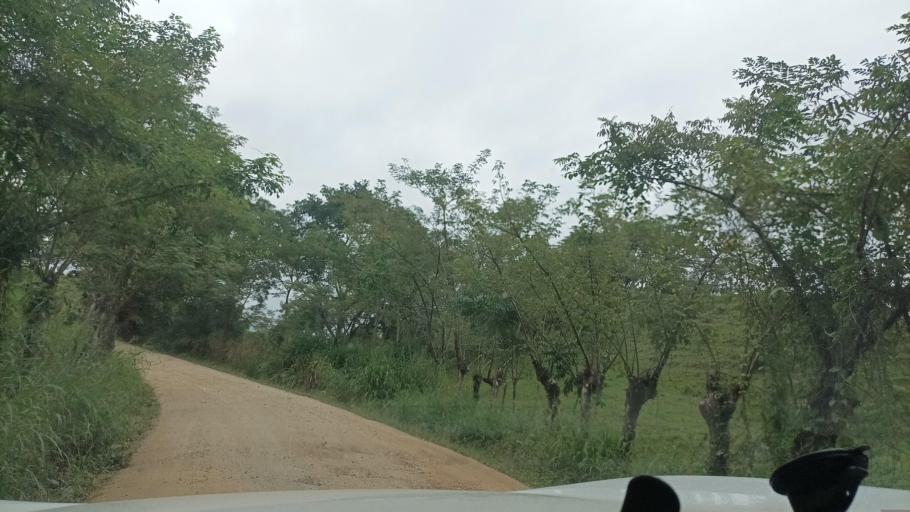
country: MX
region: Veracruz
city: Hidalgotitlan
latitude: 17.6182
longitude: -94.5155
